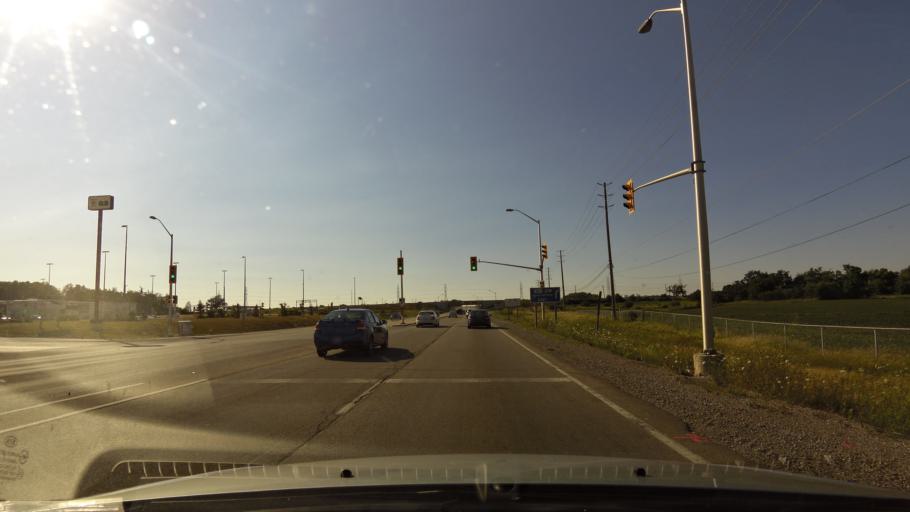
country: CA
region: Ontario
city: Oakville
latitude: 43.5059
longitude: -79.7438
